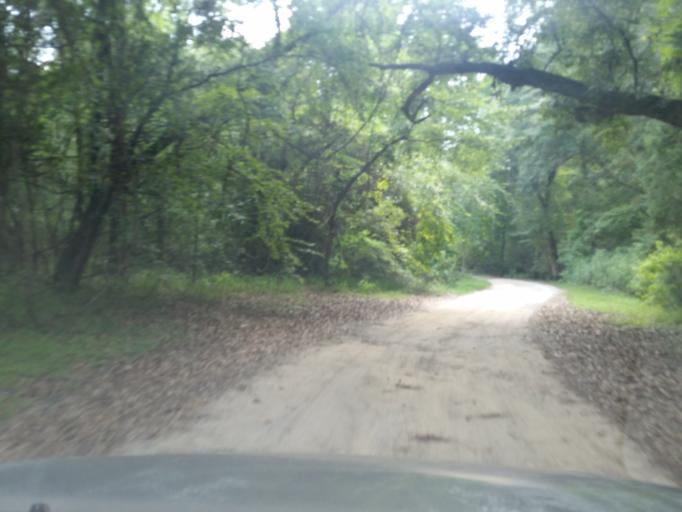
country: US
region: Alabama
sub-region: Baldwin County
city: Spanish Fort
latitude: 30.7423
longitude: -87.9229
